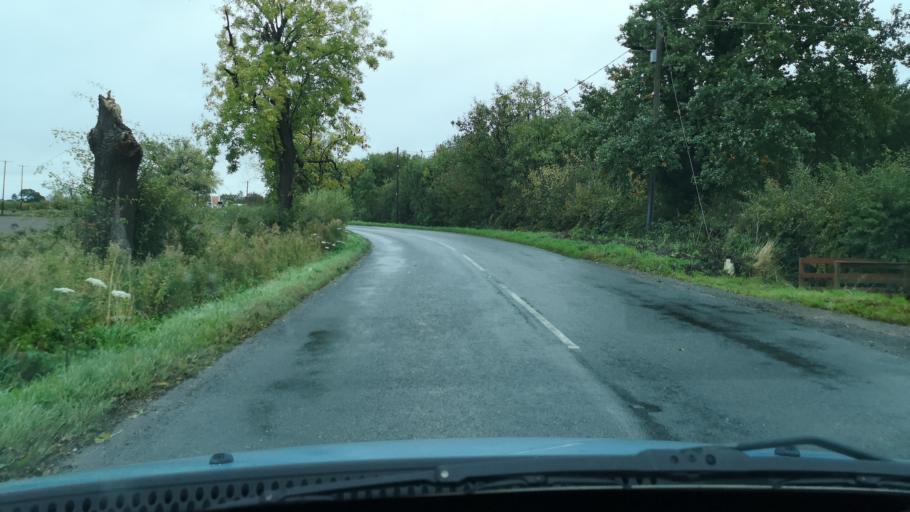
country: GB
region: England
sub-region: Doncaster
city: Moss
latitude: 53.6227
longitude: -1.1158
